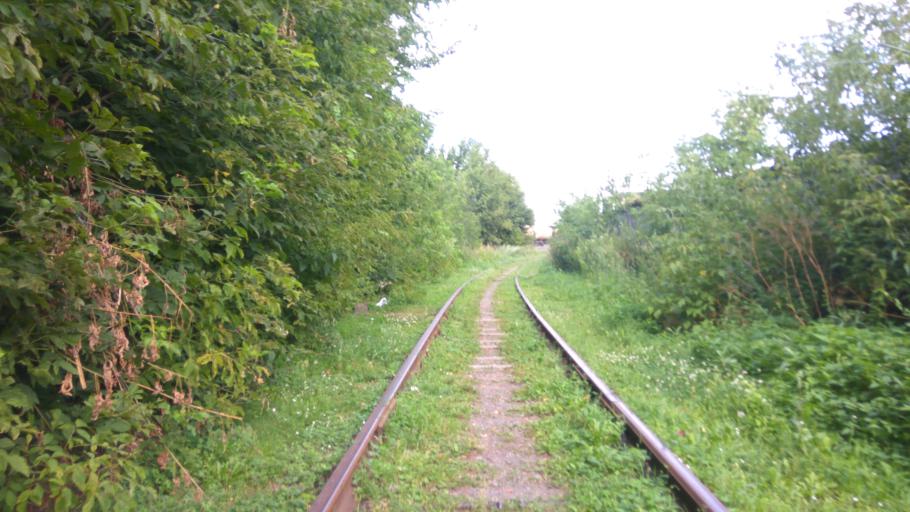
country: RU
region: Moskovskaya
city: Tomilino
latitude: 55.6714
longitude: 37.9431
